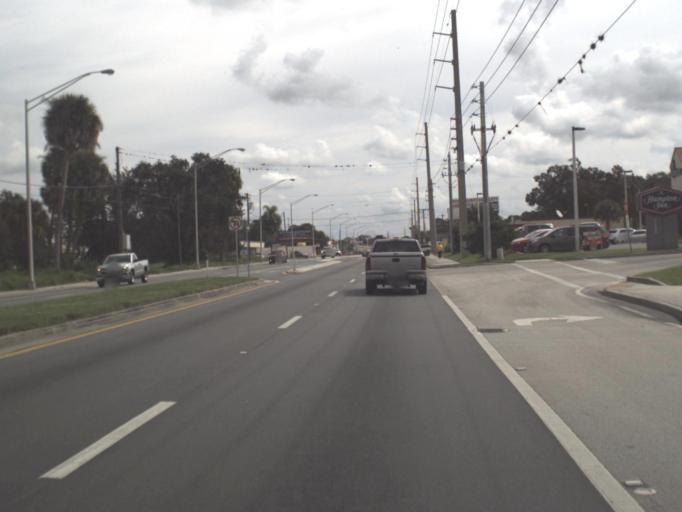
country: US
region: Florida
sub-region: Okeechobee County
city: Cypress Quarters
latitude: 27.2437
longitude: -80.8180
